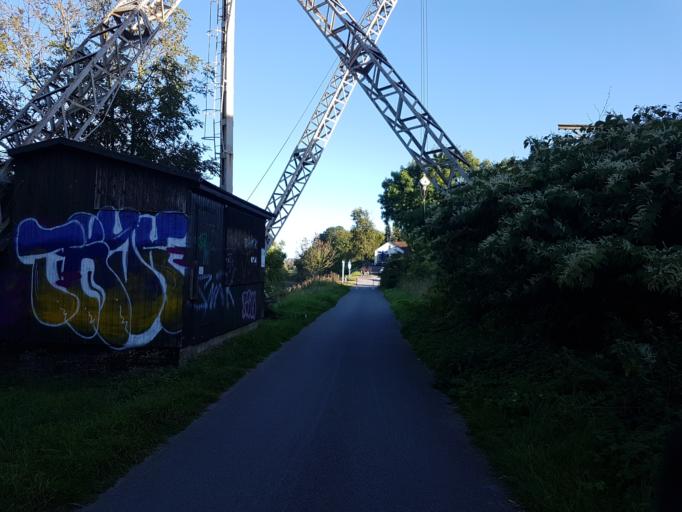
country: DE
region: North Rhine-Westphalia
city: Bad Oeynhausen
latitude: 52.2160
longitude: 8.8343
